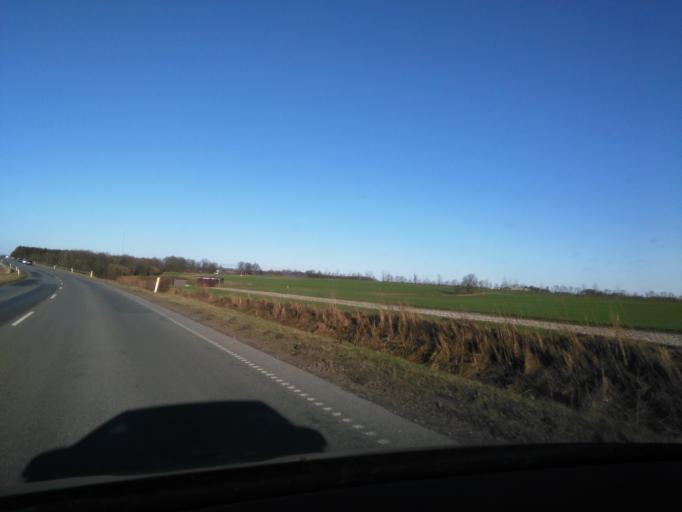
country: DK
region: North Denmark
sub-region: Mariagerfjord Kommune
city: Hobro
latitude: 56.6617
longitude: 9.8047
